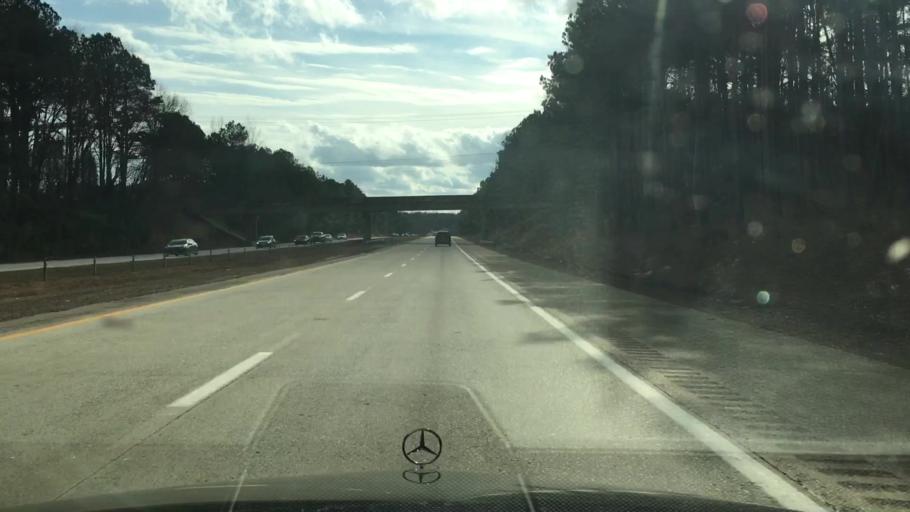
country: US
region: North Carolina
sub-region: Wake County
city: Garner
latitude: 35.5751
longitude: -78.5765
